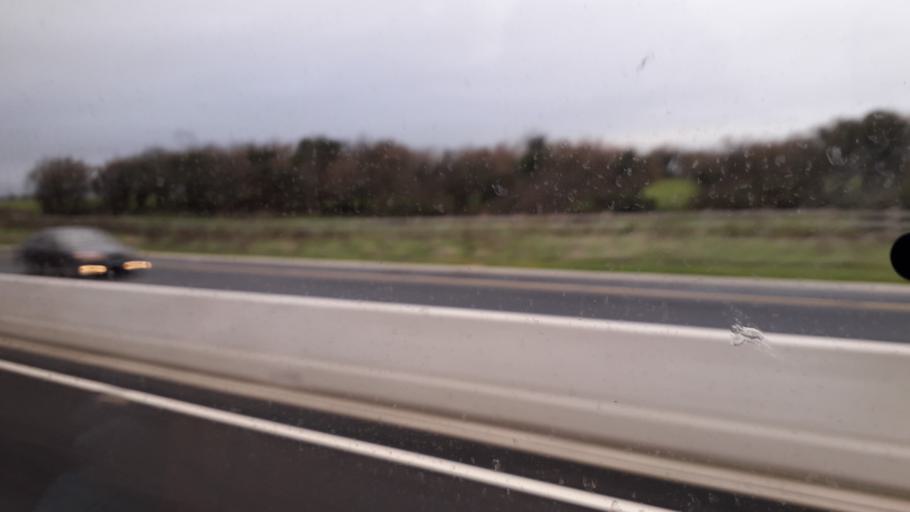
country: IE
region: Connaught
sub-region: County Galway
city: Athenry
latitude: 53.2872
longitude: -8.8058
